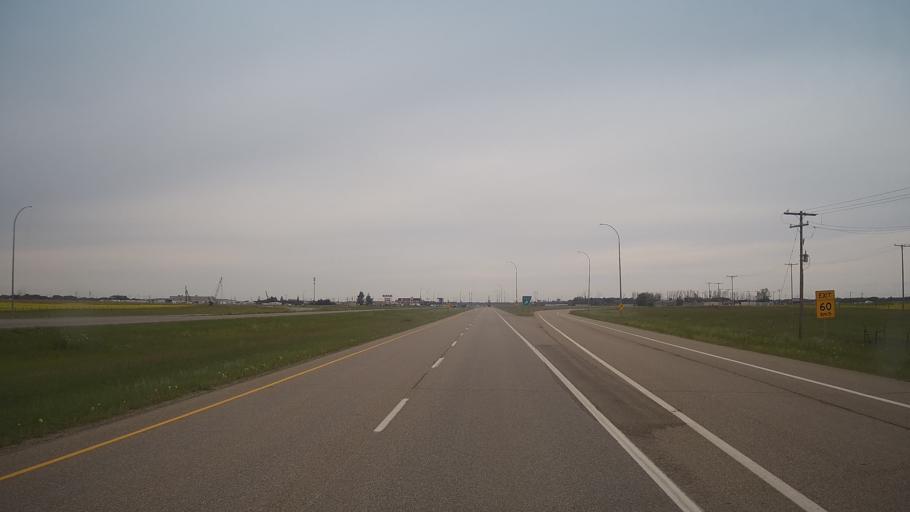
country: CA
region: Saskatchewan
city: Saskatoon
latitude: 52.0484
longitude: -106.5941
